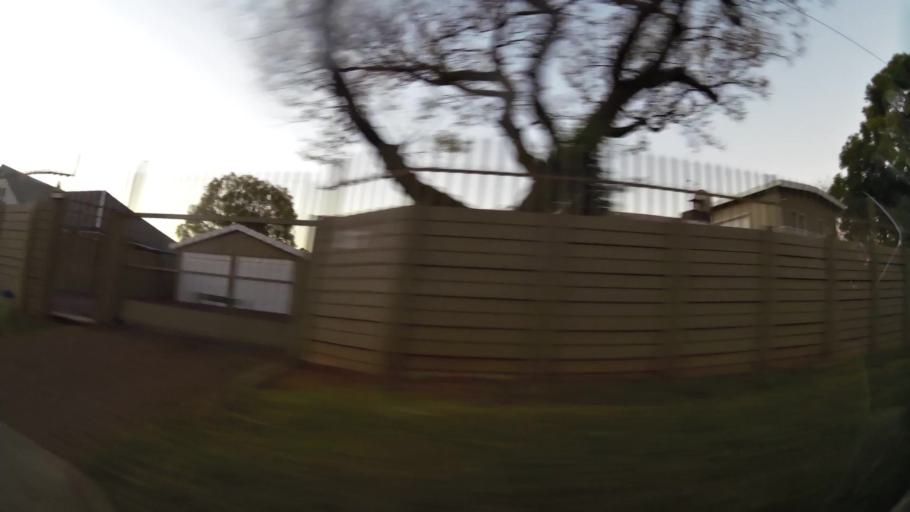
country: ZA
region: Gauteng
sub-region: City of Johannesburg Metropolitan Municipality
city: Roodepoort
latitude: -26.1702
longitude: 27.9194
